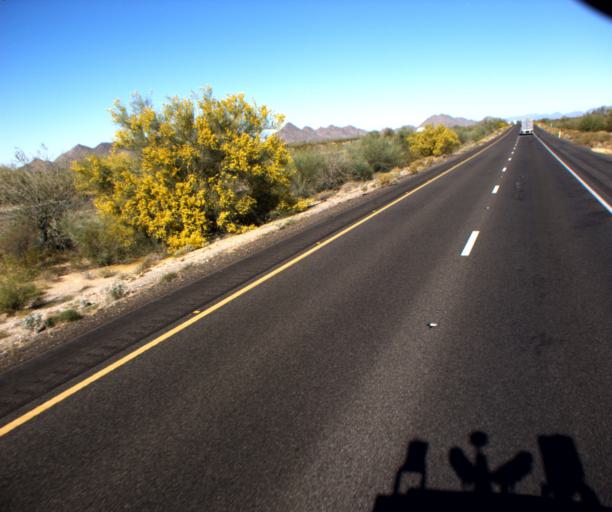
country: US
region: Arizona
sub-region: Maricopa County
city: Gila Bend
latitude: 32.8825
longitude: -112.4609
